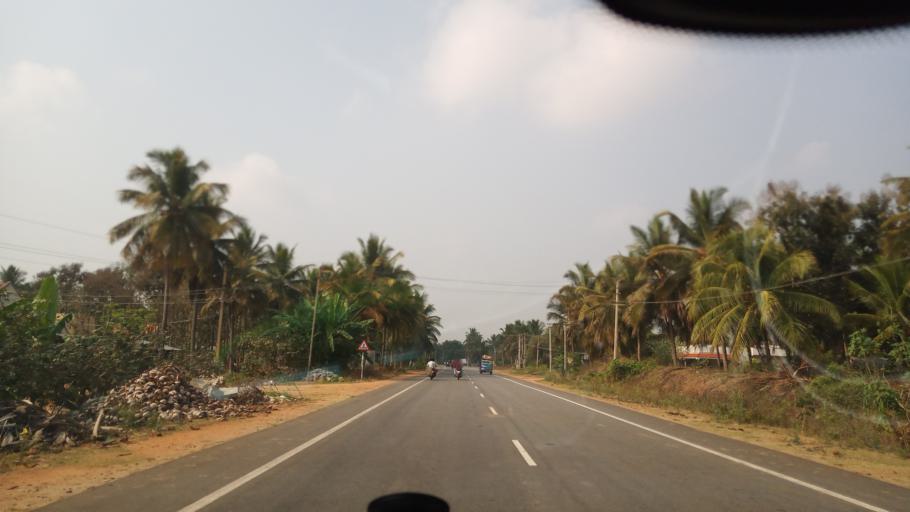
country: IN
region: Karnataka
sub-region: Mandya
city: Nagamangala
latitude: 12.7710
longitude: 76.7400
